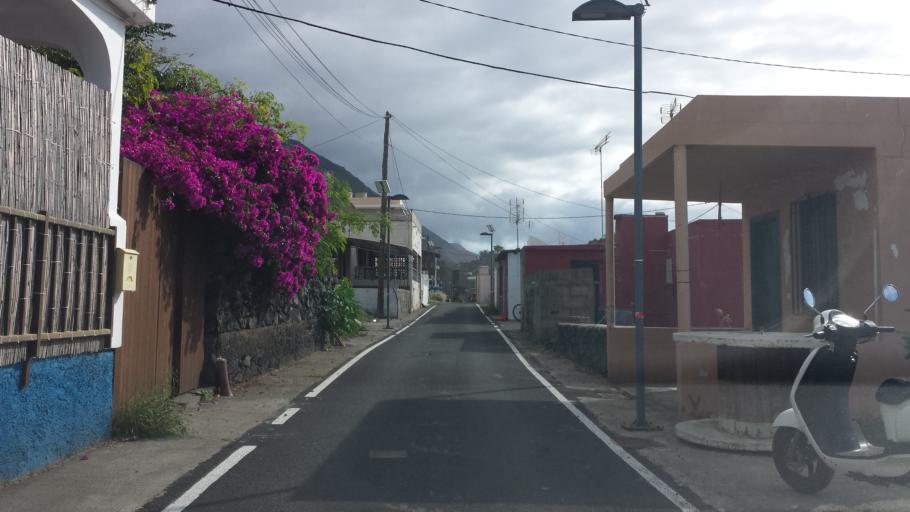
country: ES
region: Canary Islands
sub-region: Provincia de Santa Cruz de Tenerife
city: Fuencaliente de la Palma
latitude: 28.5534
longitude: -17.8887
